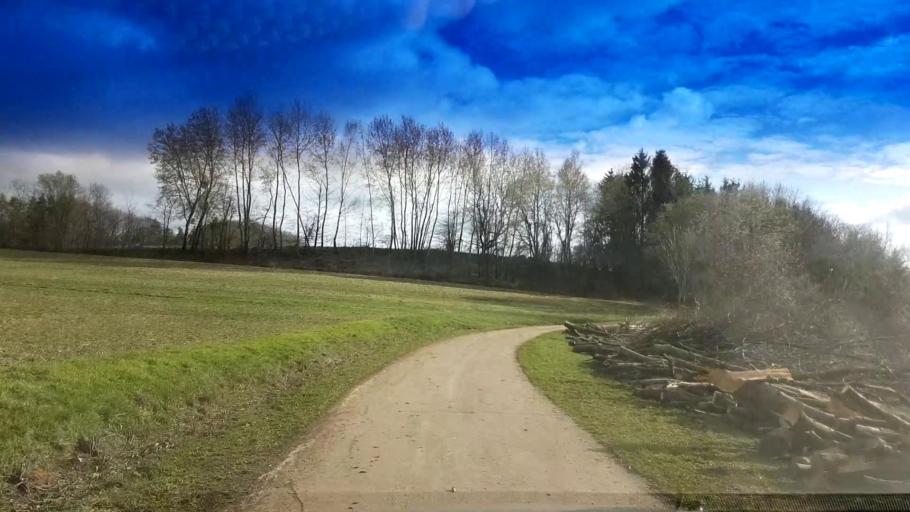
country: DE
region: Bavaria
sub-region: Upper Franconia
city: Schesslitz
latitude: 50.0098
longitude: 11.0355
